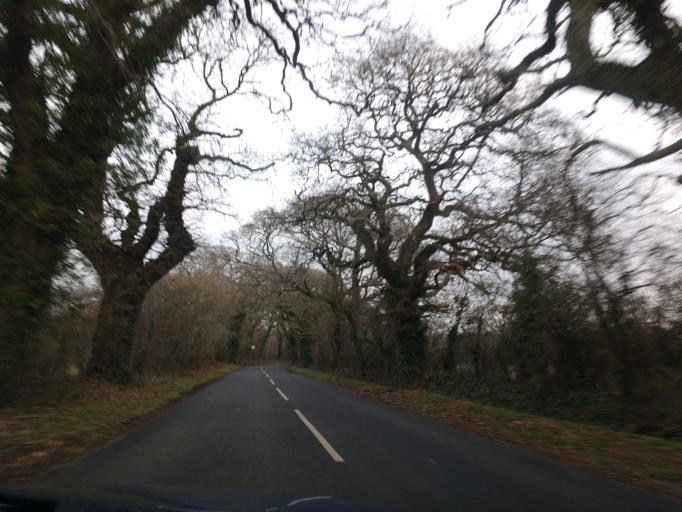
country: GB
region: England
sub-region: Isle of Wight
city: Shalfleet
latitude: 50.7108
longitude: -1.3813
